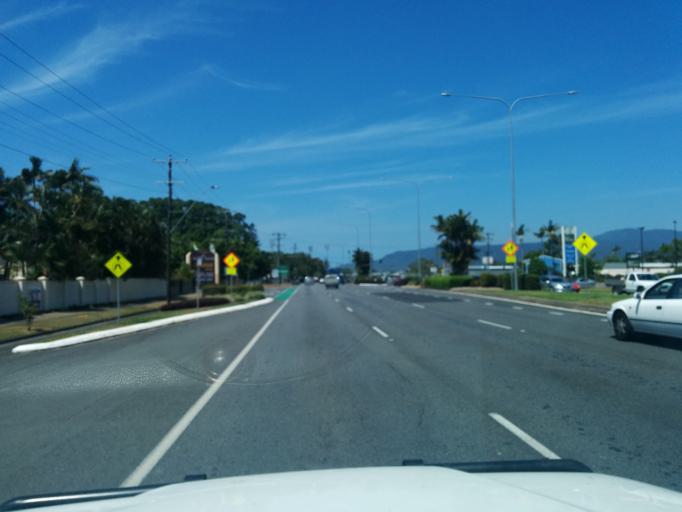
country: AU
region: Queensland
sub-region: Cairns
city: Woree
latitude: -16.9398
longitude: 145.7431
